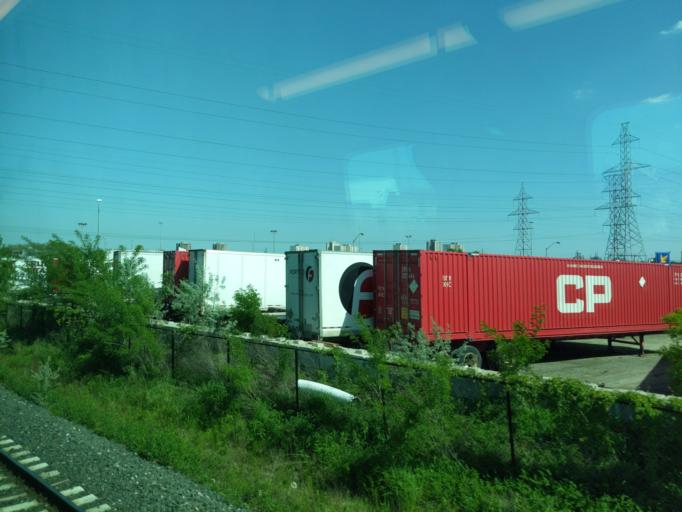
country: CA
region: Ontario
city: Etobicoke
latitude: 43.7062
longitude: -79.5673
